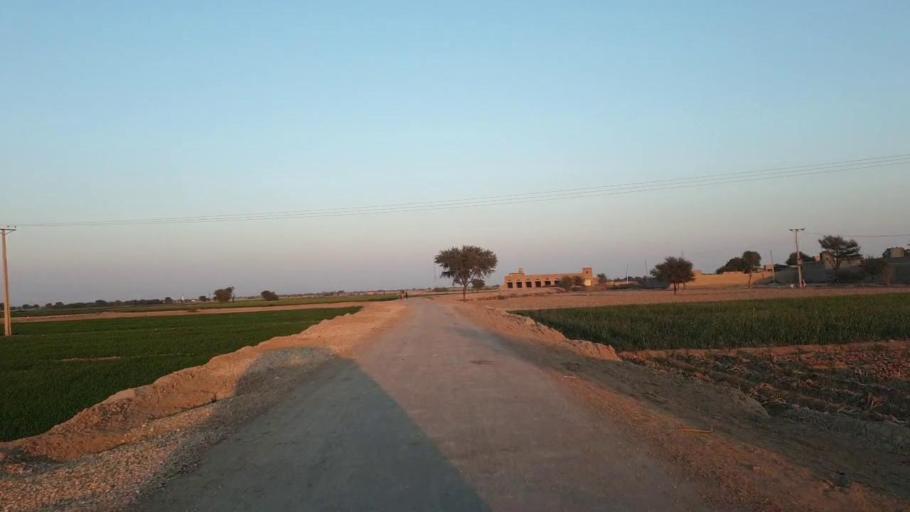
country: PK
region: Sindh
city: Shahpur Chakar
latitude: 26.1657
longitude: 68.5455
